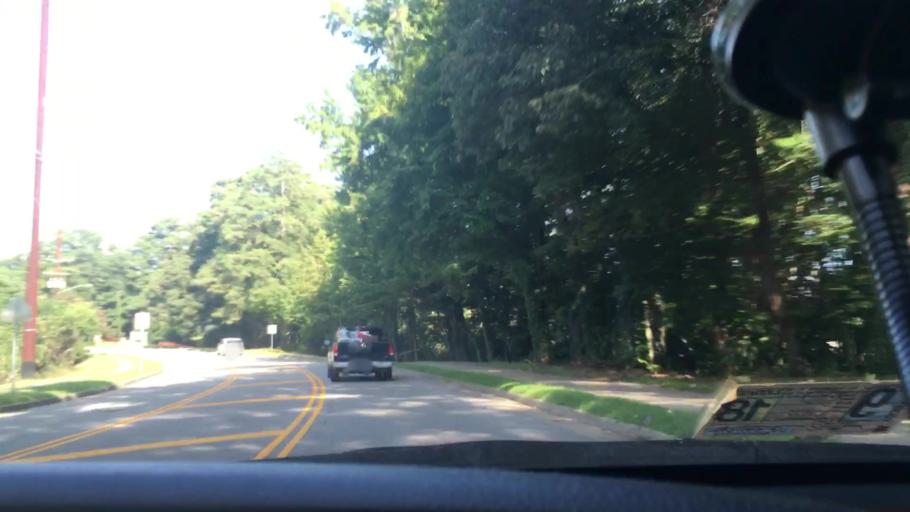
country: US
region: Virginia
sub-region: City of Virginia Beach
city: Virginia Beach
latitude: 36.8793
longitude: -76.0340
